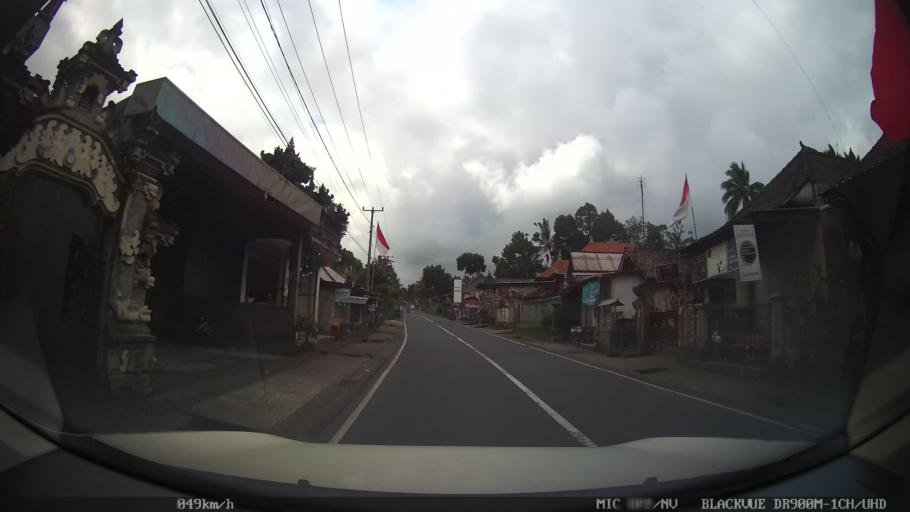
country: ID
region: Bali
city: Banjar Kubu
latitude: -8.3929
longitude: 115.4198
